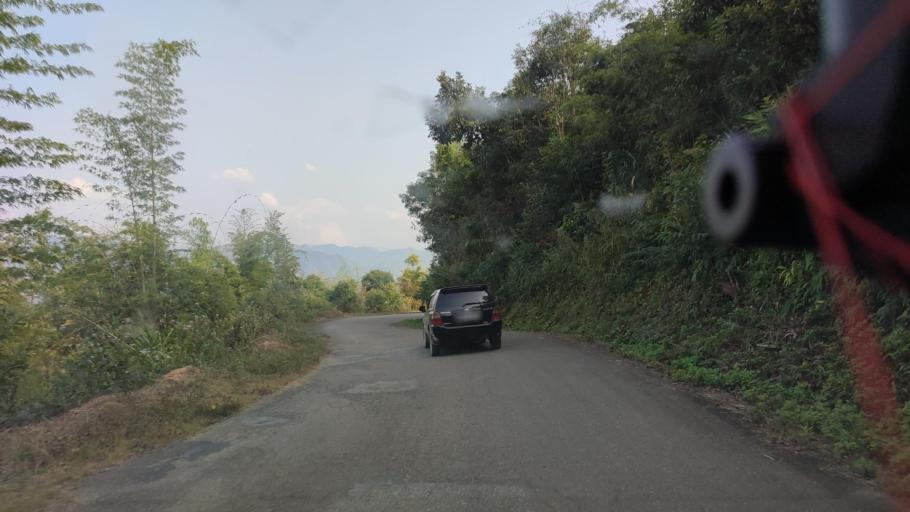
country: CN
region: Yunnan
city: Menghai
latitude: 21.4837
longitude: 99.7421
